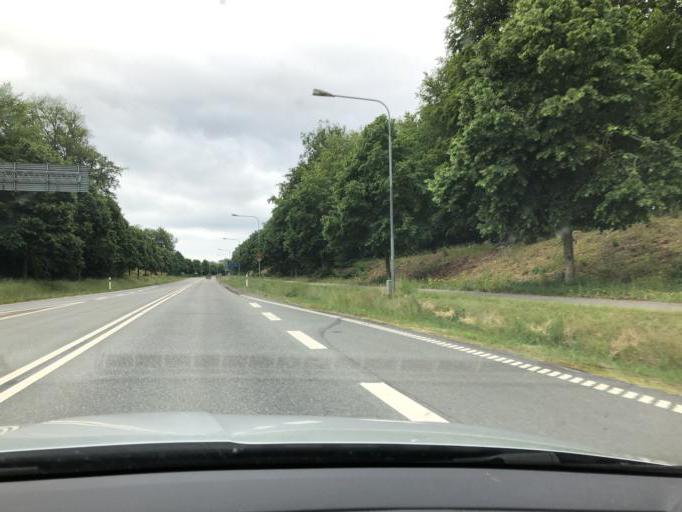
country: SE
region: Blekinge
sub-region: Solvesborgs Kommun
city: Soelvesborg
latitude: 56.0643
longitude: 14.5974
